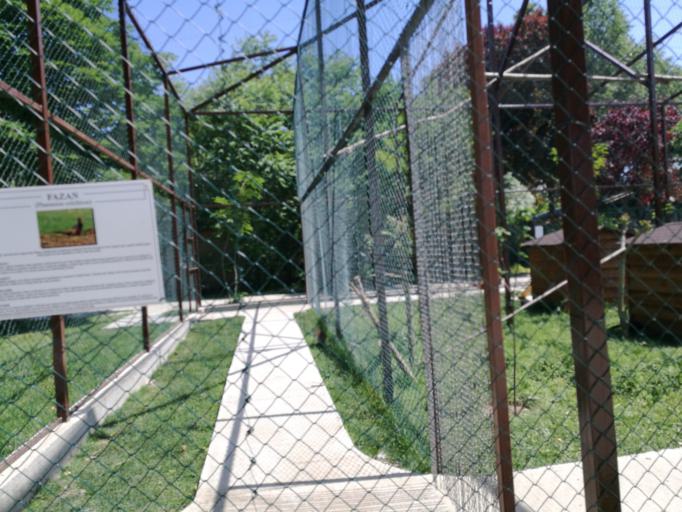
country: RO
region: Constanta
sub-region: Municipiul Constanta
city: Constanta
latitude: 44.2046
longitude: 28.6413
